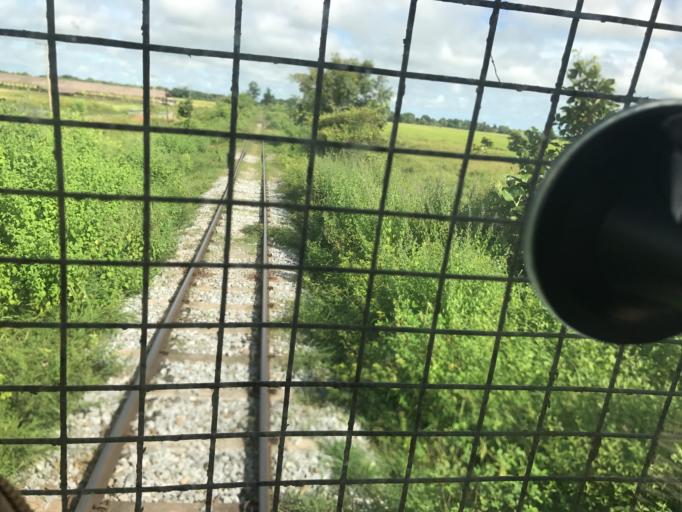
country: MM
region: Bago
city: Letpandan
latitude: 18.1031
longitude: 95.6786
